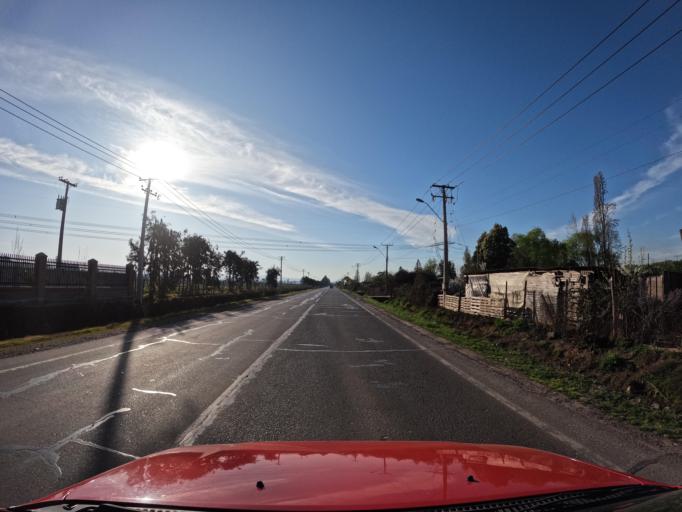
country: CL
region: Maule
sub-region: Provincia de Curico
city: Teno
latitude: -34.8815
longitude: -71.0784
